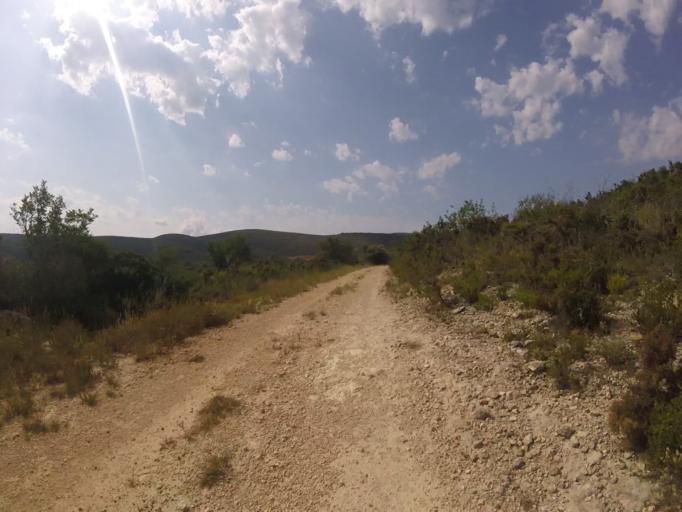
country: ES
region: Valencia
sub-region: Provincia de Castello
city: Alcala de Xivert
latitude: 40.3381
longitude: 0.1964
